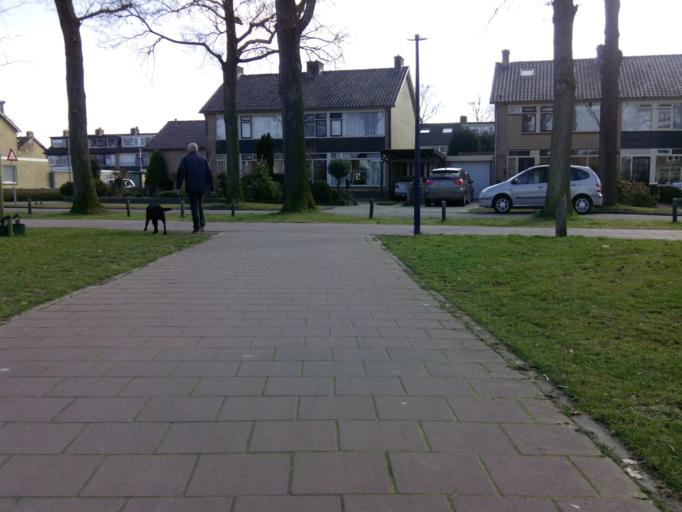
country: NL
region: Utrecht
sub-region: Gemeente Utrechtse Heuvelrug
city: Overberg
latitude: 52.0846
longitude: 5.4800
